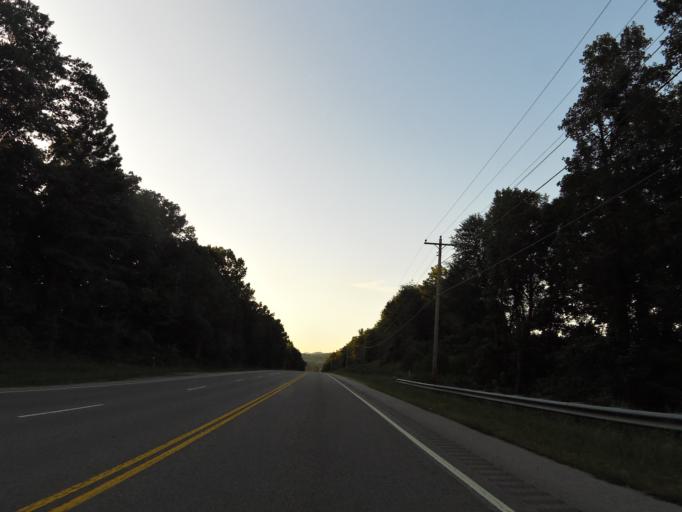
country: US
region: Tennessee
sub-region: Roane County
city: Midtown
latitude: 35.8399
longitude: -84.5422
